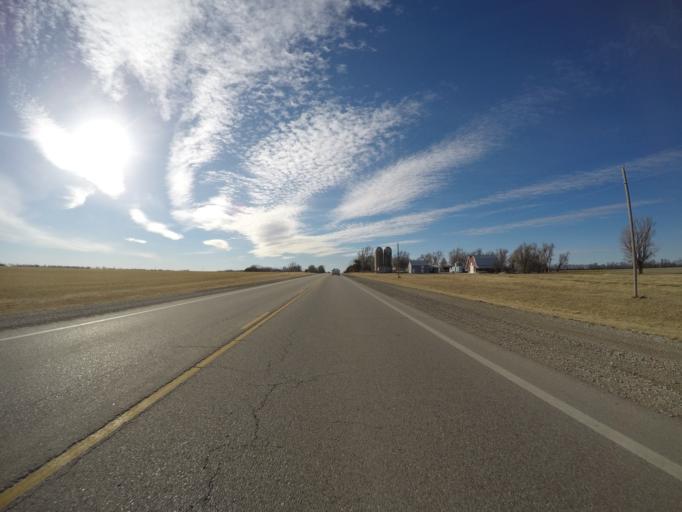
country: US
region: Kansas
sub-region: McPherson County
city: McPherson
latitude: 38.3768
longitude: -97.5515
